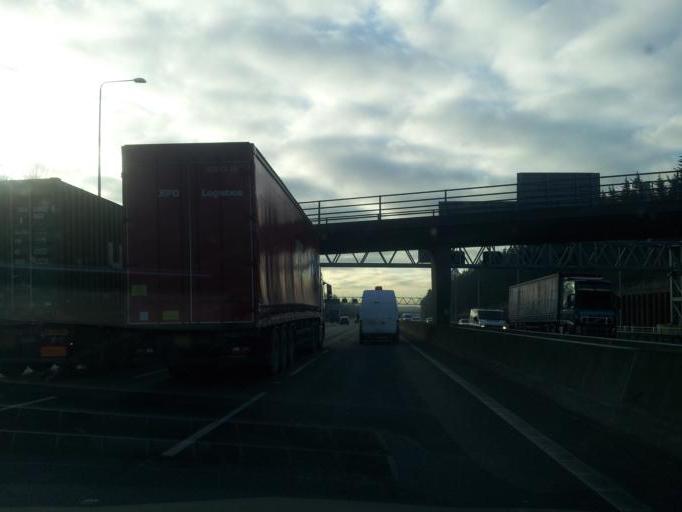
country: GB
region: England
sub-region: Hertfordshire
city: Kings Langley
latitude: 51.6909
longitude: -0.4469
